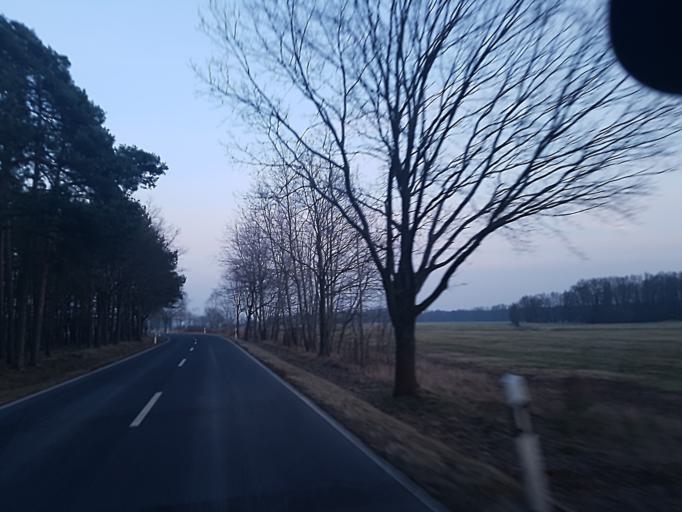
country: DE
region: Saxony-Anhalt
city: Holzdorf
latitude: 51.7509
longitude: 13.1472
